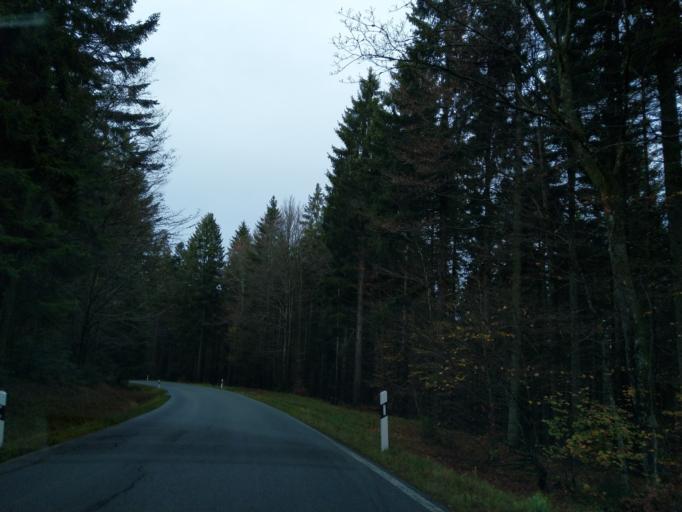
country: DE
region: Bavaria
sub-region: Lower Bavaria
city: Schofweg
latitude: 48.8218
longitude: 13.2372
